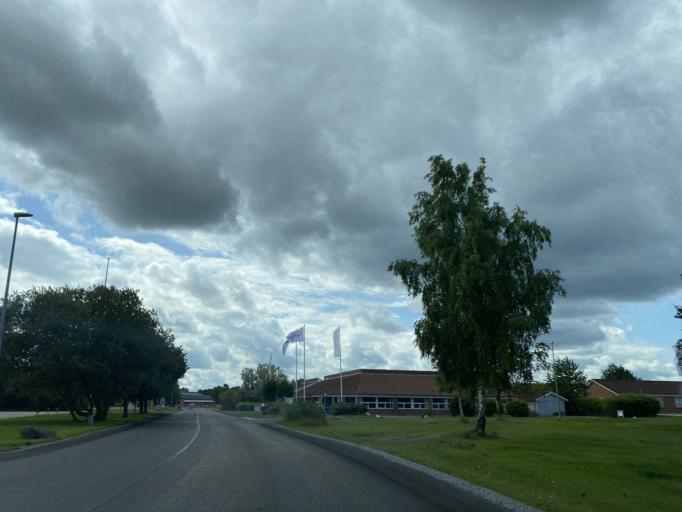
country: DK
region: Central Jutland
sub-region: Silkeborg Kommune
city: Silkeborg
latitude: 56.2045
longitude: 9.5780
